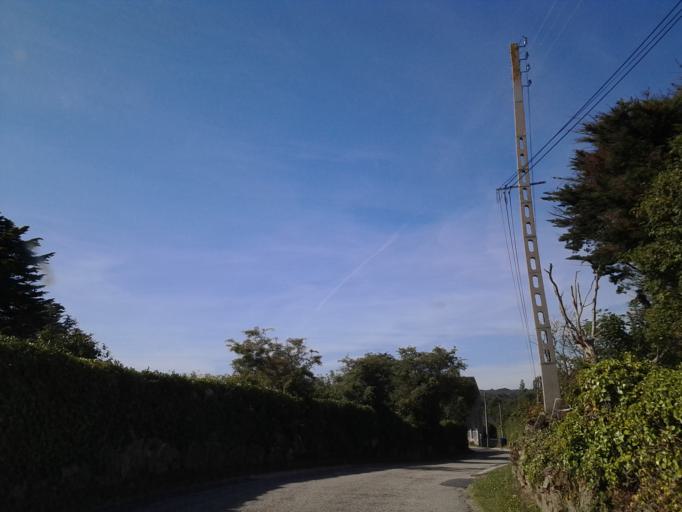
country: FR
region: Lower Normandy
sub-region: Departement de la Manche
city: Fermanville
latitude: 49.6825
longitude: -1.4577
